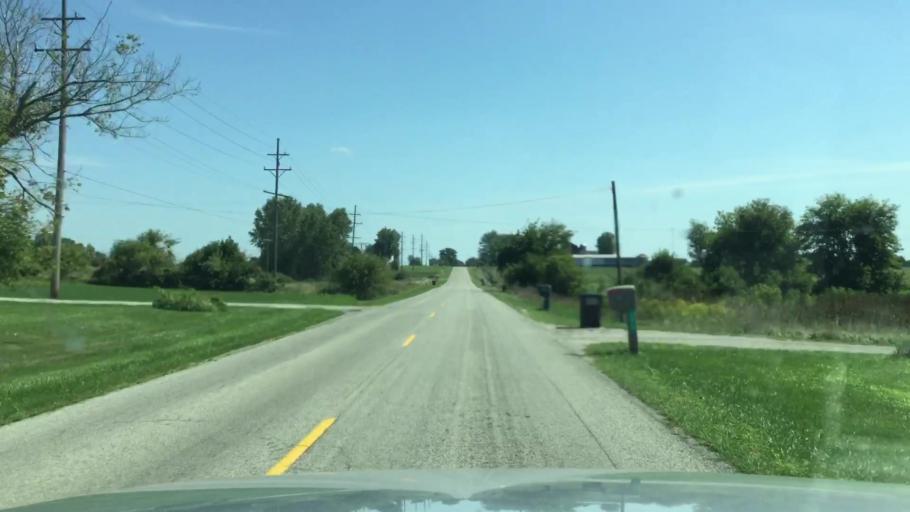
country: US
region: Michigan
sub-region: Lenawee County
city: Clinton
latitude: 42.0653
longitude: -83.9483
